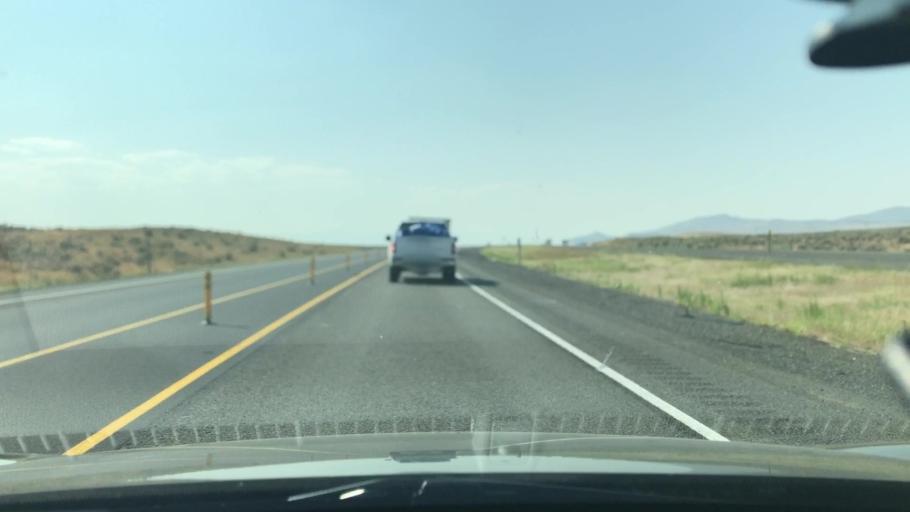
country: US
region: Oregon
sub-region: Baker County
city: Baker City
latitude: 44.6886
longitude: -117.6811
